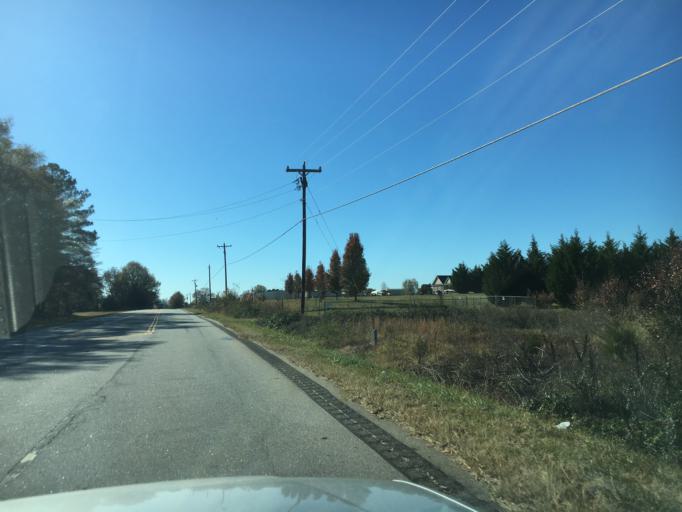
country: US
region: South Carolina
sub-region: Anderson County
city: Centerville
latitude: 34.5032
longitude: -82.7688
